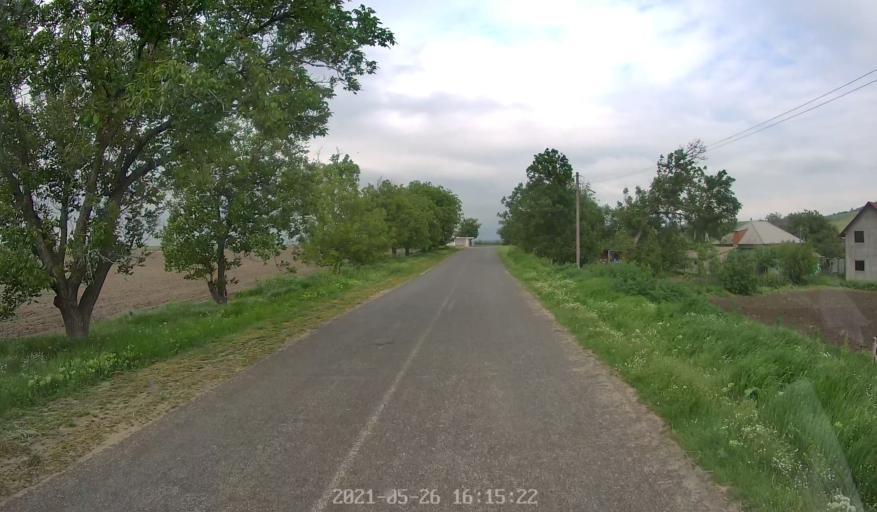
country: MD
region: Hincesti
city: Dancu
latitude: 46.7169
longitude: 28.3467
